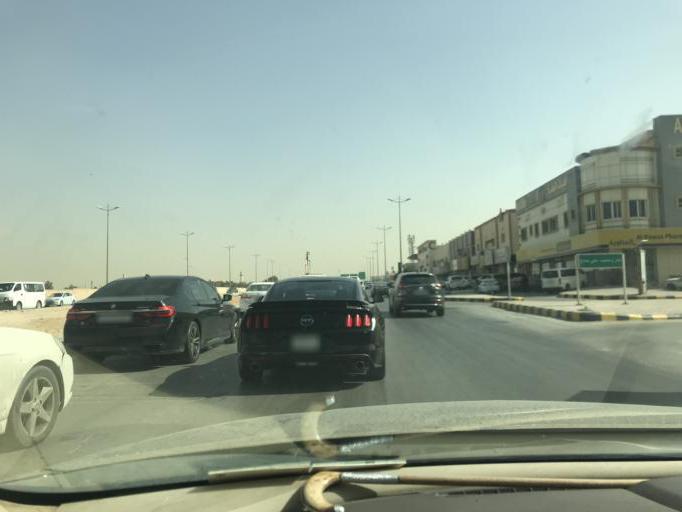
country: SA
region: Ar Riyad
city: Riyadh
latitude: 24.7914
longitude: 46.7445
